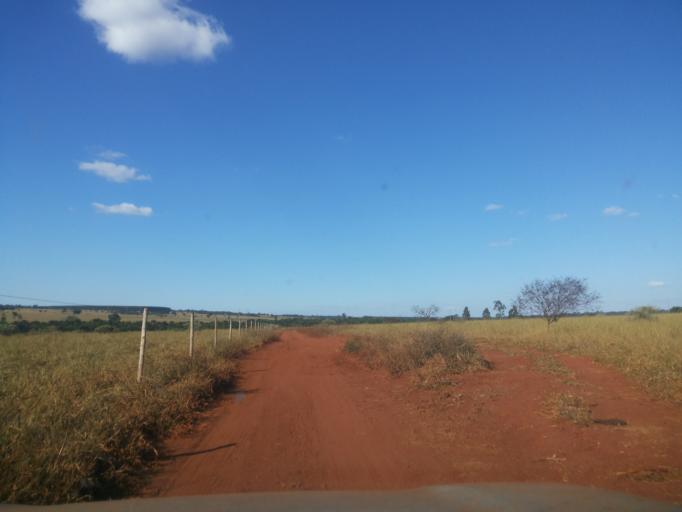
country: BR
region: Minas Gerais
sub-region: Centralina
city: Centralina
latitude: -18.7364
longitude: -49.1761
